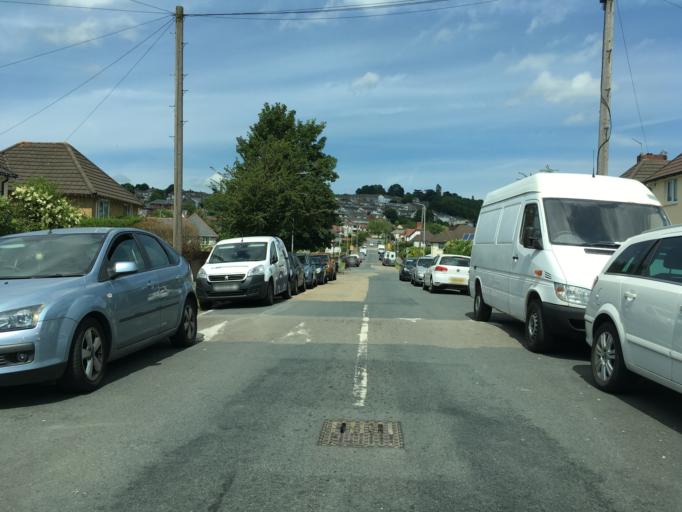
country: GB
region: Wales
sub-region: Newport
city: Caerleon
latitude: 51.5854
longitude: -2.9617
